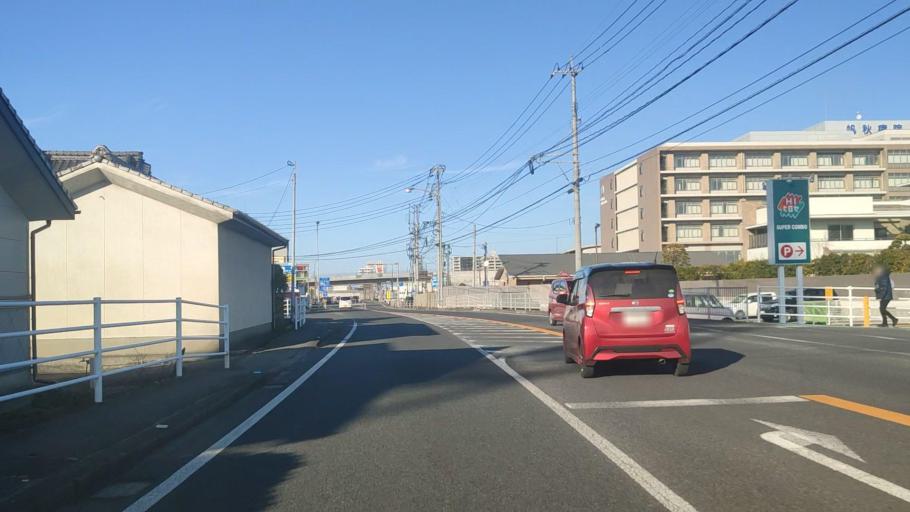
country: JP
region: Oita
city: Oita
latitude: 33.2235
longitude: 131.6186
